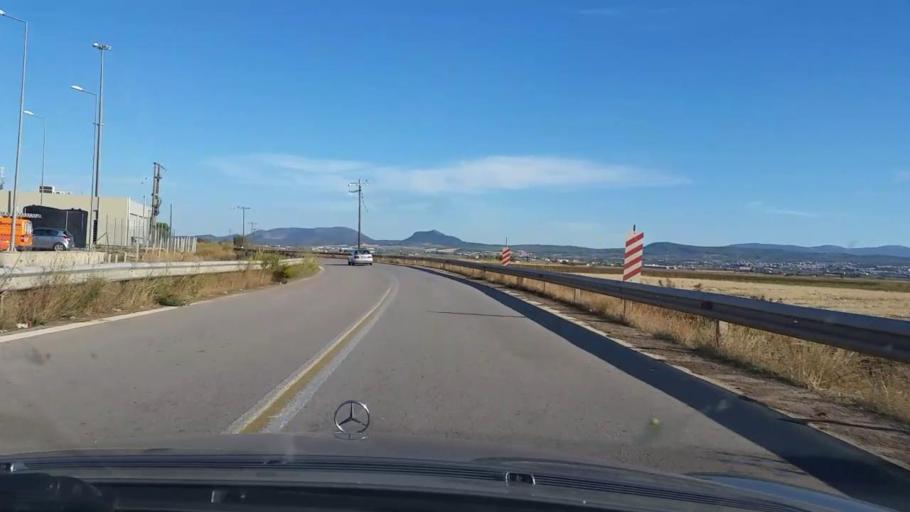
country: GR
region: Central Greece
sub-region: Nomos Voiotias
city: Thivai
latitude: 38.3706
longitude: 23.2857
